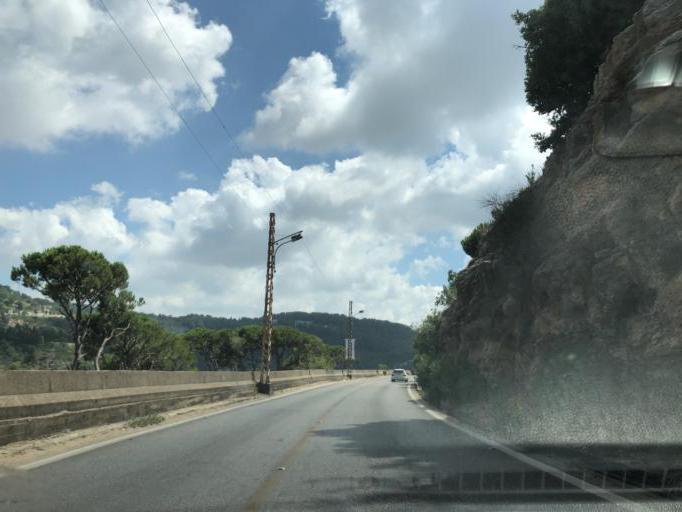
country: LB
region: Mont-Liban
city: Beit ed Dine
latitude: 33.6999
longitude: 35.5756
